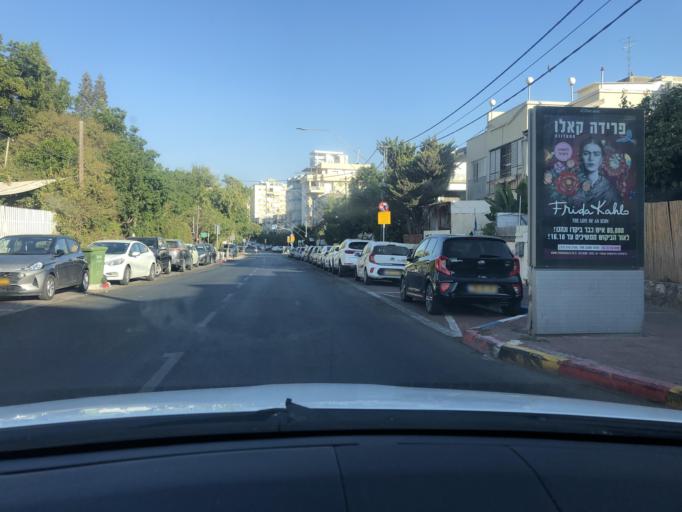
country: IL
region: Tel Aviv
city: Giv`atayim
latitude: 32.0620
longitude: 34.8244
